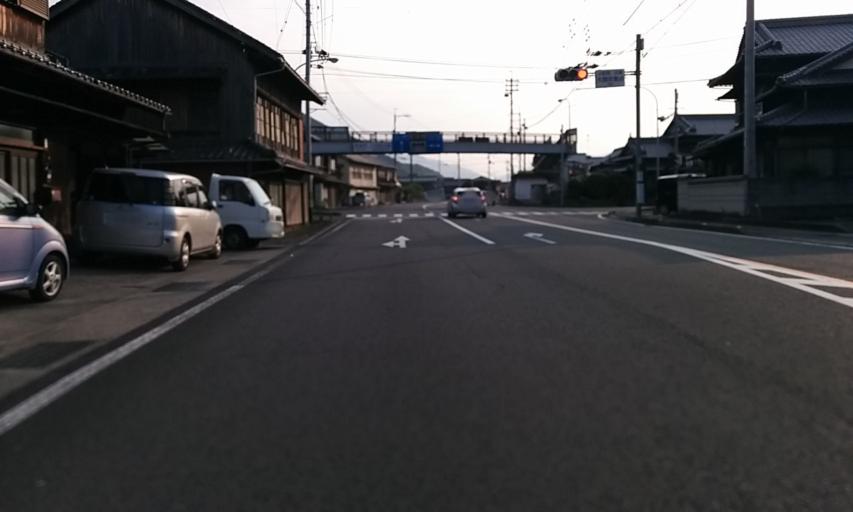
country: JP
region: Ehime
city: Saijo
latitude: 33.8823
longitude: 133.0780
